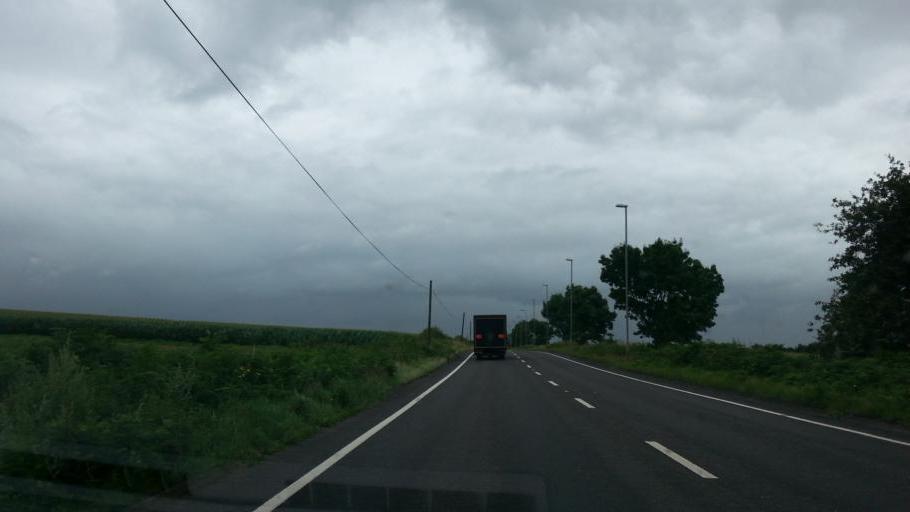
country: GB
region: England
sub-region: Nottinghamshire
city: Bilsthorpe
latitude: 53.1364
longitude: -1.0503
